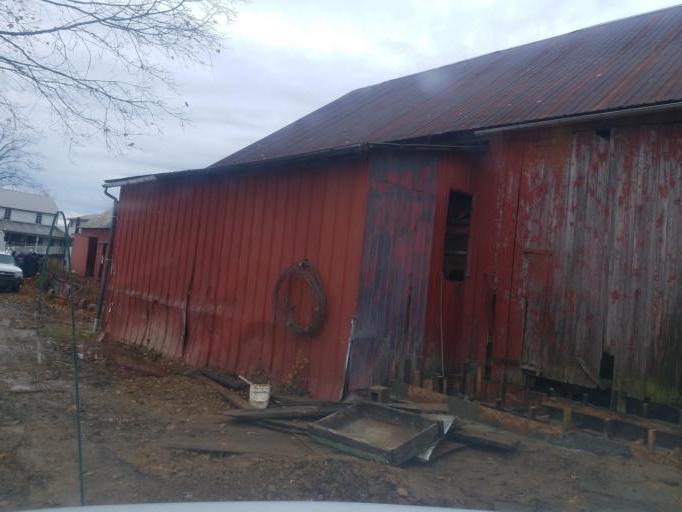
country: US
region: Ohio
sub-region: Morgan County
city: McConnelsville
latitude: 39.5190
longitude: -81.8358
